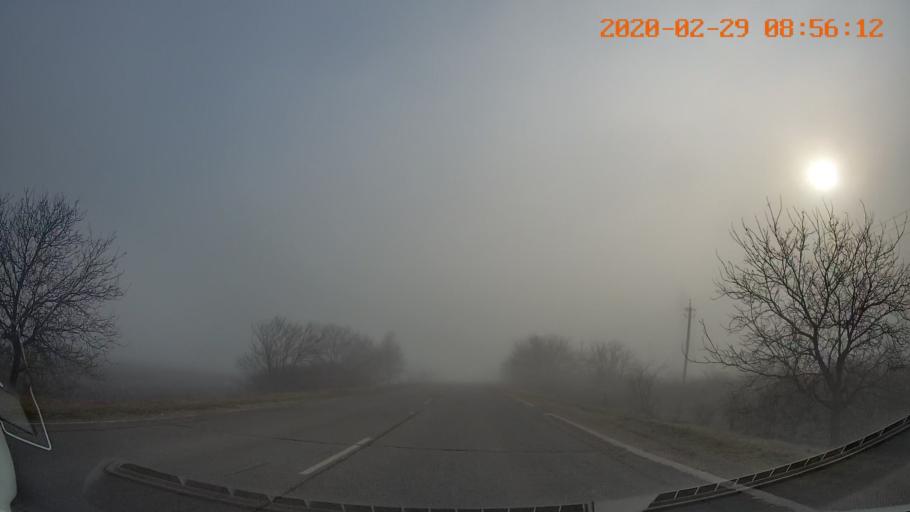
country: MD
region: Telenesti
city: Tiraspolul Nou
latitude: 46.9294
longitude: 29.6053
